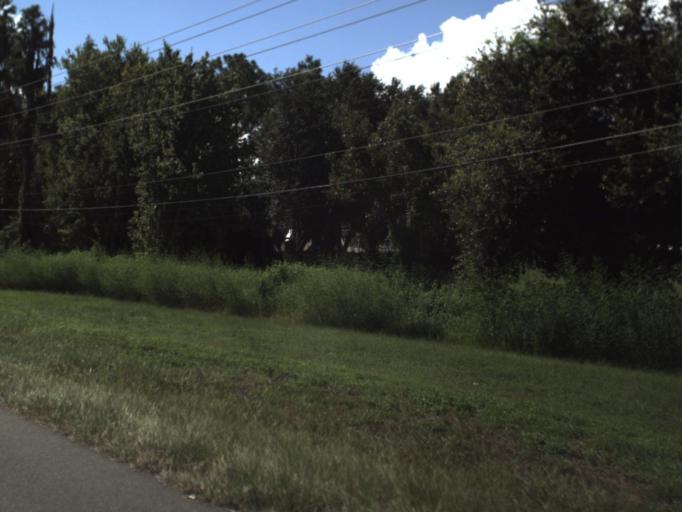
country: US
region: Florida
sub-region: Polk County
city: Kathleen
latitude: 28.1825
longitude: -81.9950
